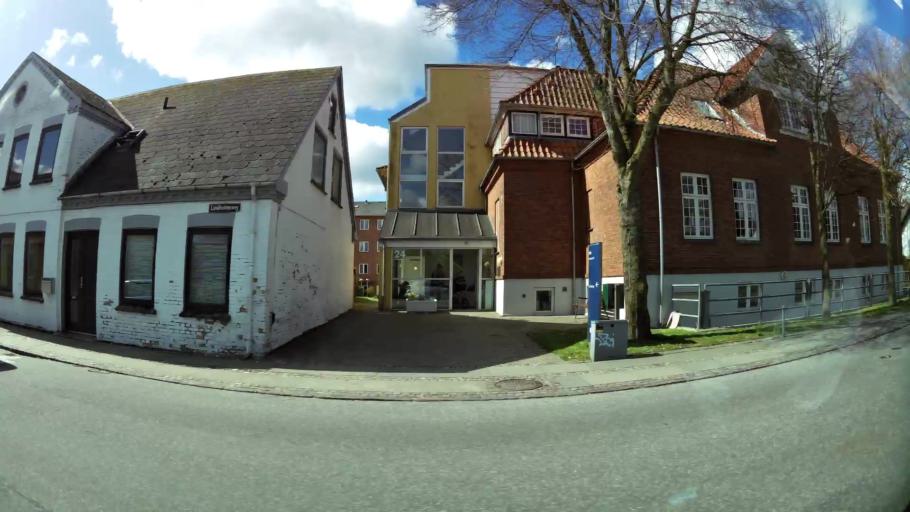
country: DK
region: North Denmark
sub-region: Alborg Kommune
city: Aalborg
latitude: 57.0627
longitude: 9.9161
